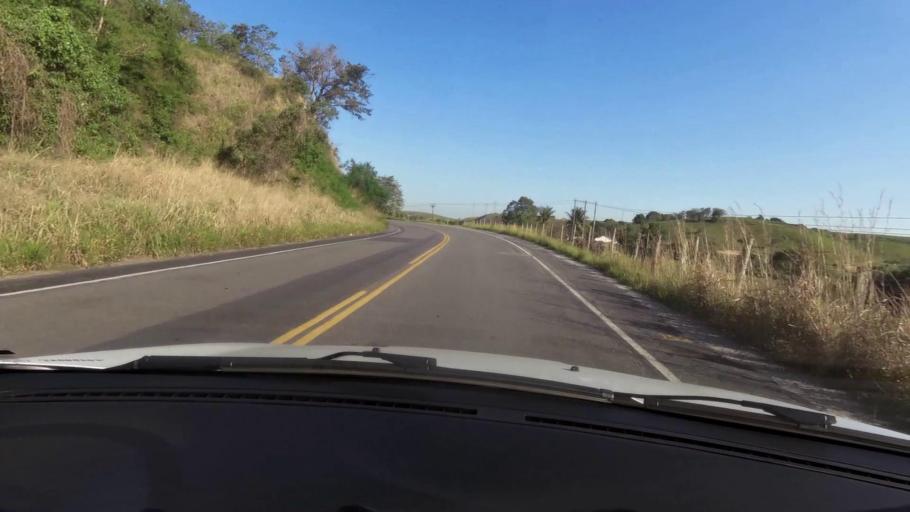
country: BR
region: Espirito Santo
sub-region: Alfredo Chaves
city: Alfredo Chaves
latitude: -20.7108
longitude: -40.6696
